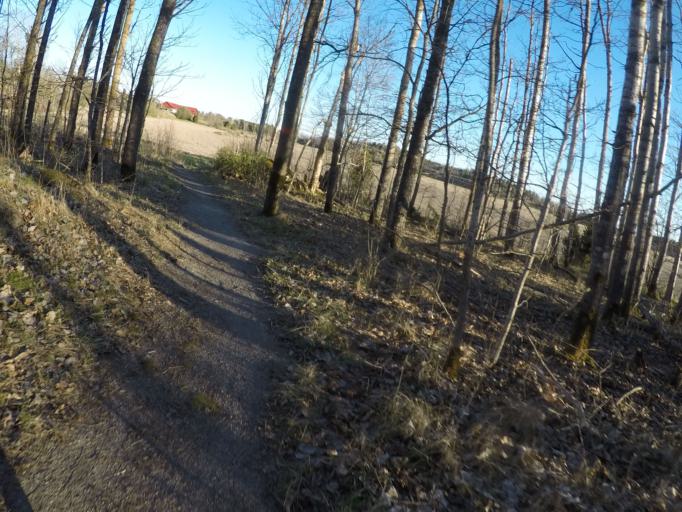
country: SE
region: Soedermanland
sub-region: Eskilstuna Kommun
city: Eskilstuna
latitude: 59.4018
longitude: 16.5228
